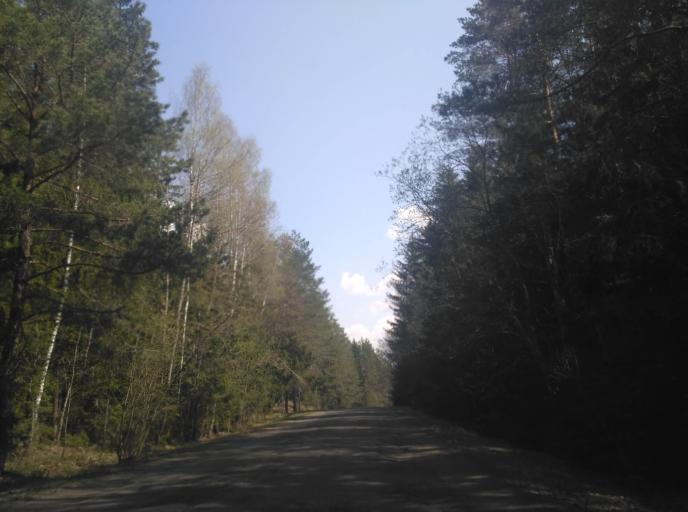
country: BY
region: Minsk
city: Loshnitsa
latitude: 54.4939
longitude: 28.7082
